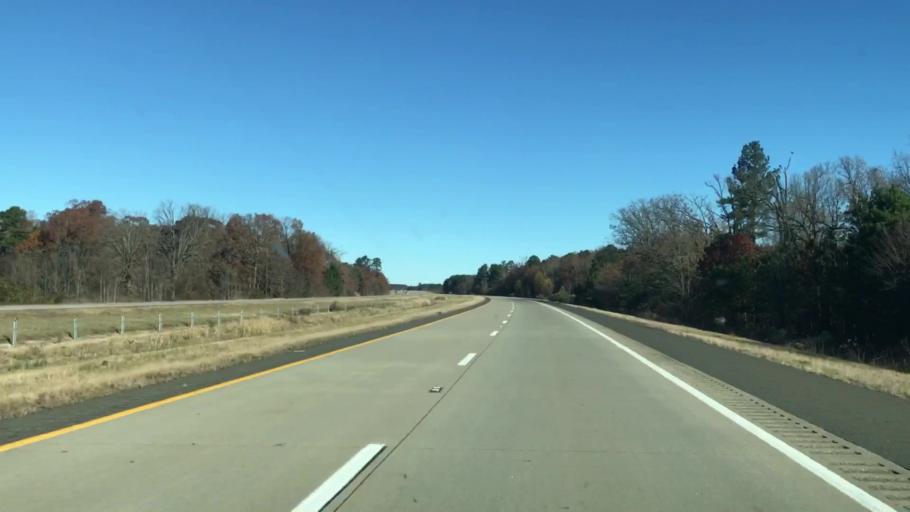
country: US
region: Texas
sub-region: Bowie County
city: Texarkana
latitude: 33.2118
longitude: -93.8739
